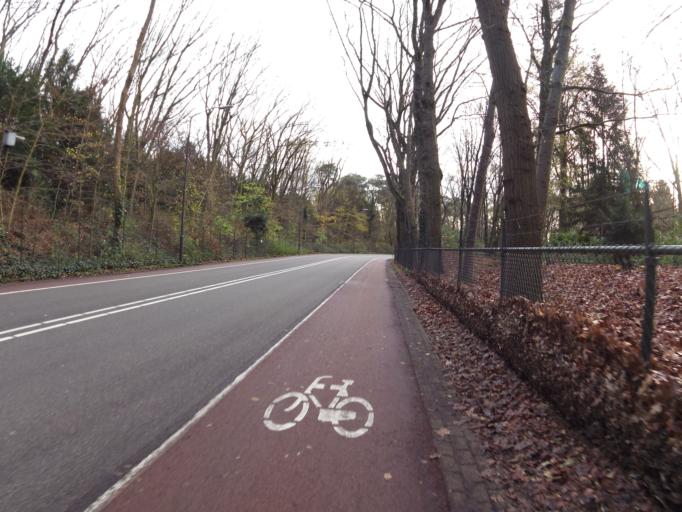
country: NL
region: North Brabant
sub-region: Gemeente Vught
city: Vught
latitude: 51.6473
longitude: 5.2729
